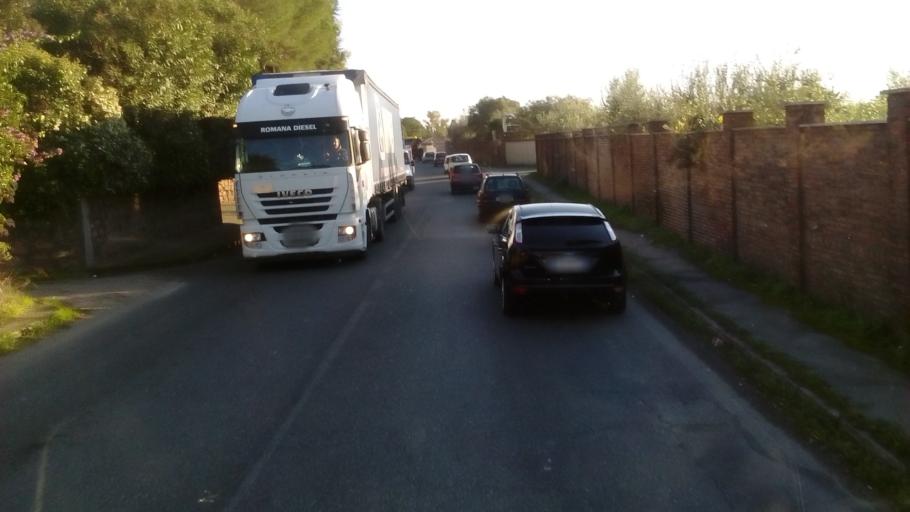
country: IT
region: Latium
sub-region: Citta metropolitana di Roma Capitale
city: Pavona
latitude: 41.7248
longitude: 12.6183
